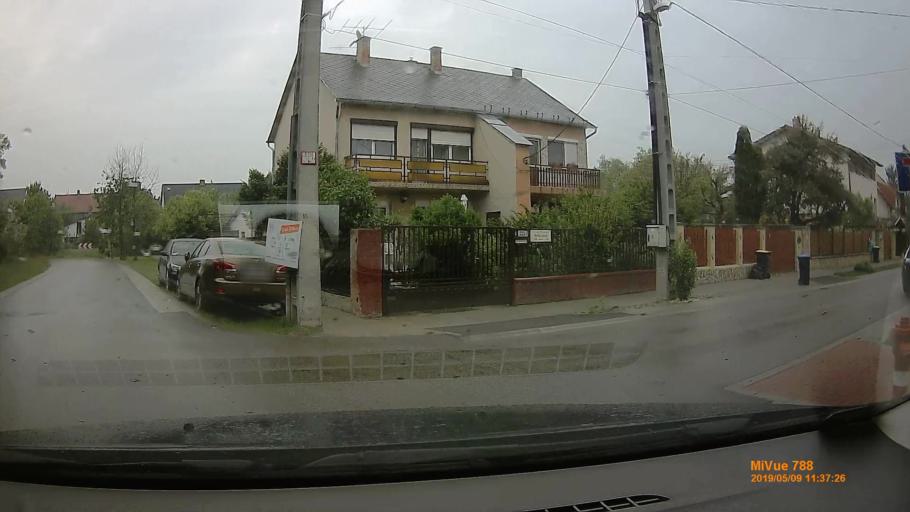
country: HU
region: Budapest
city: Budapest XVI. keruelet
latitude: 47.5307
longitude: 19.1848
